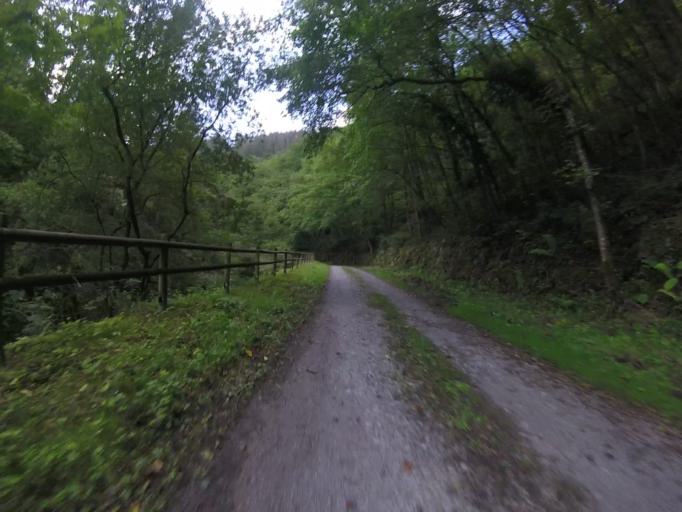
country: ES
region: Basque Country
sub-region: Provincia de Guipuzcoa
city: Elduayen
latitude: 43.1639
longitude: -1.9696
